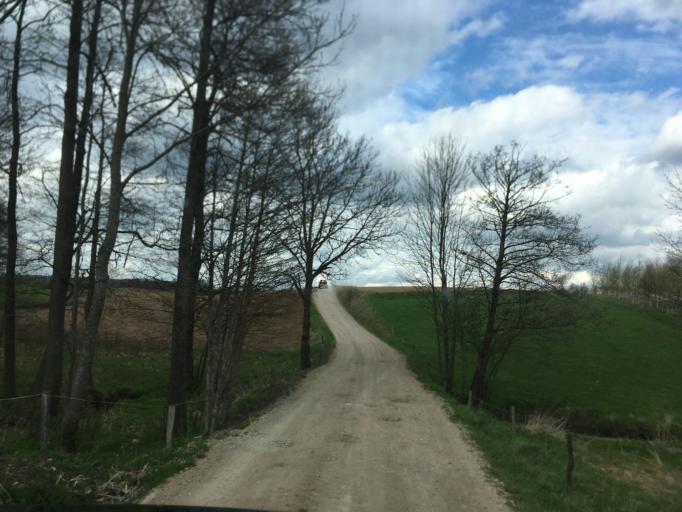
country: PL
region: Podlasie
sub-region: Powiat sejnenski
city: Punsk
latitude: 54.3789
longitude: 22.9567
